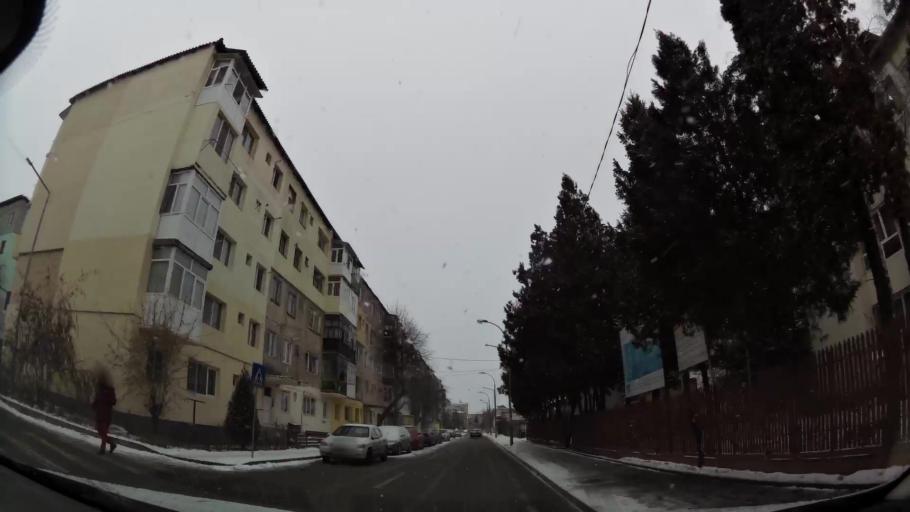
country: RO
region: Dambovita
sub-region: Municipiul Targoviste
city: Targoviste
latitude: 44.9243
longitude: 25.4456
